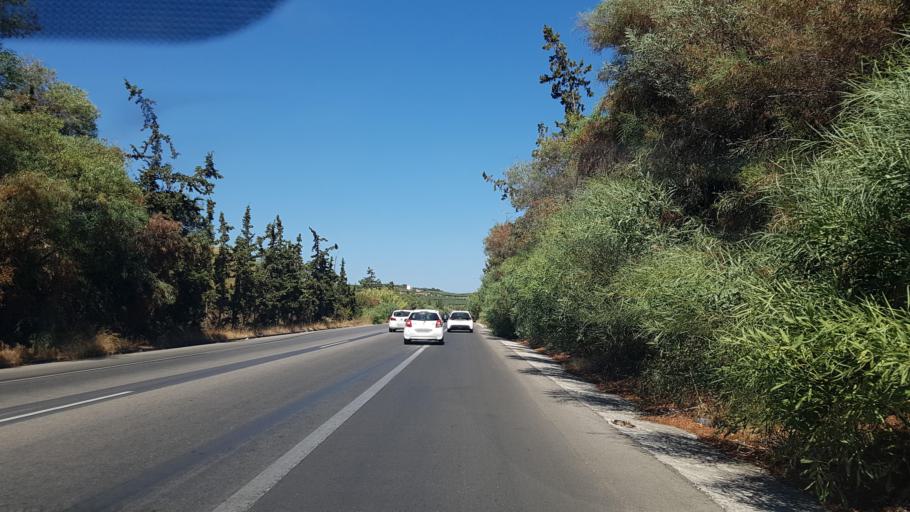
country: GR
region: Crete
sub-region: Nomos Chanias
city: Gerani
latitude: 35.5150
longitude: 23.8492
